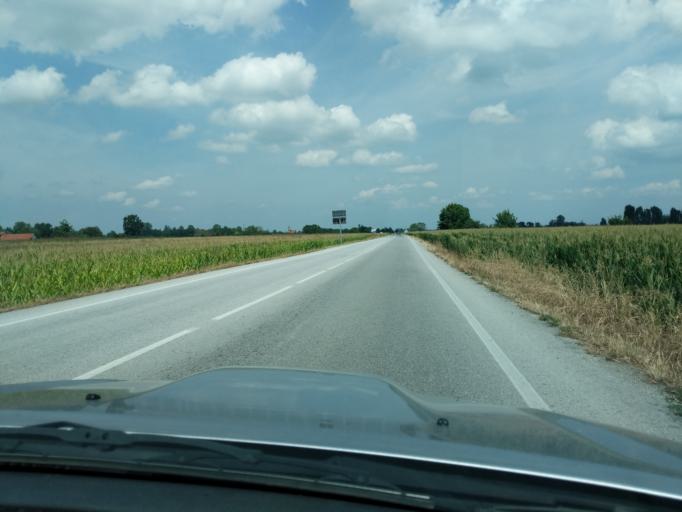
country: IT
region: Piedmont
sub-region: Provincia di Cuneo
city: Cuneo
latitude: 44.3989
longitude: 7.5828
